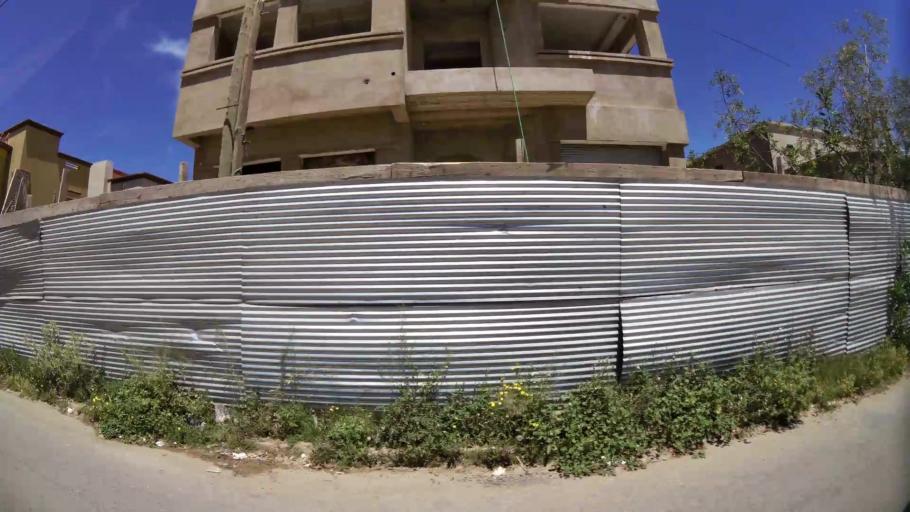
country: MA
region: Oriental
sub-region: Oujda-Angad
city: Oujda
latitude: 34.6602
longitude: -1.9440
